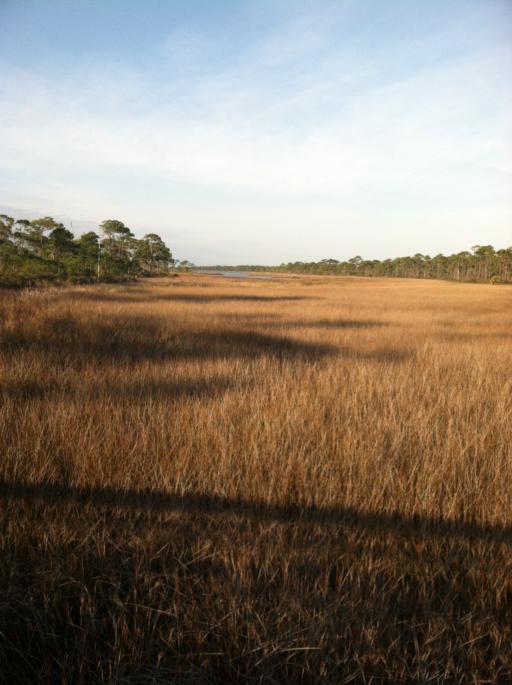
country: US
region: Florida
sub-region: Franklin County
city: Eastpoint
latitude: 29.7134
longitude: -84.7560
